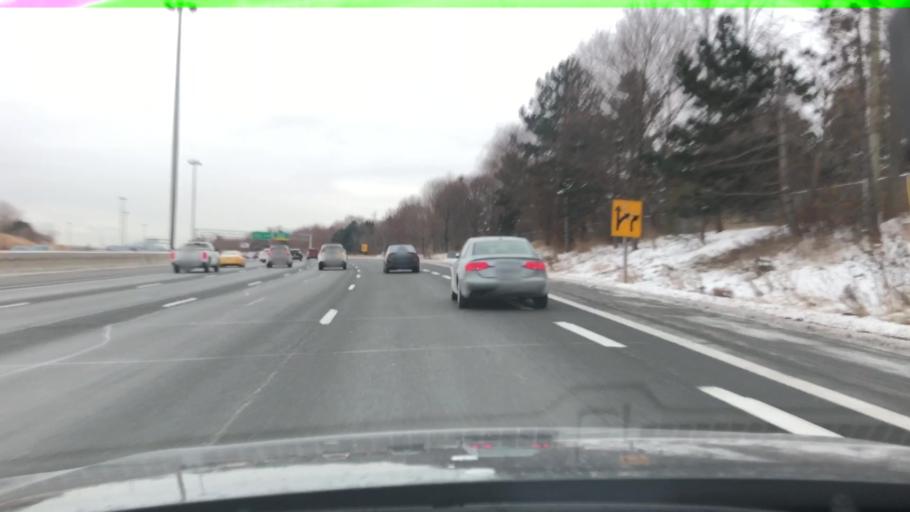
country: CA
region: Ontario
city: Willowdale
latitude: 43.8183
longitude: -79.3601
